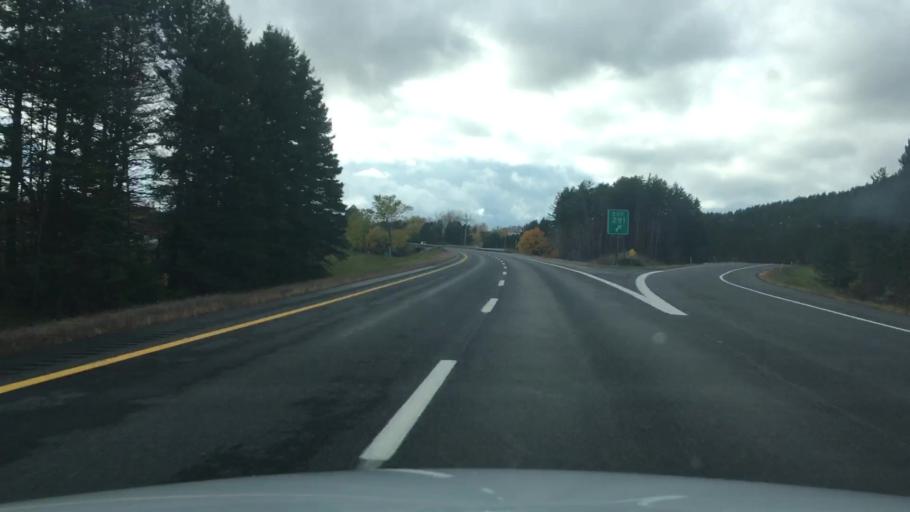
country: US
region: Maine
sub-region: Aroostook County
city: Hodgdon
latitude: 46.1453
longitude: -68.0570
